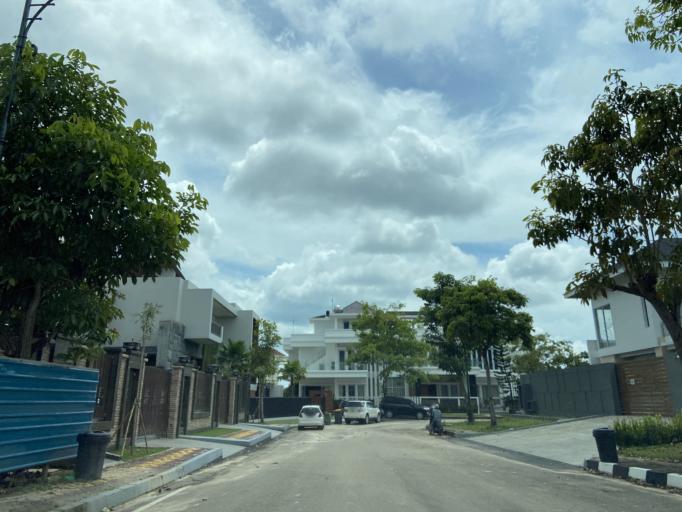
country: SG
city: Singapore
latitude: 1.1272
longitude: 104.0007
